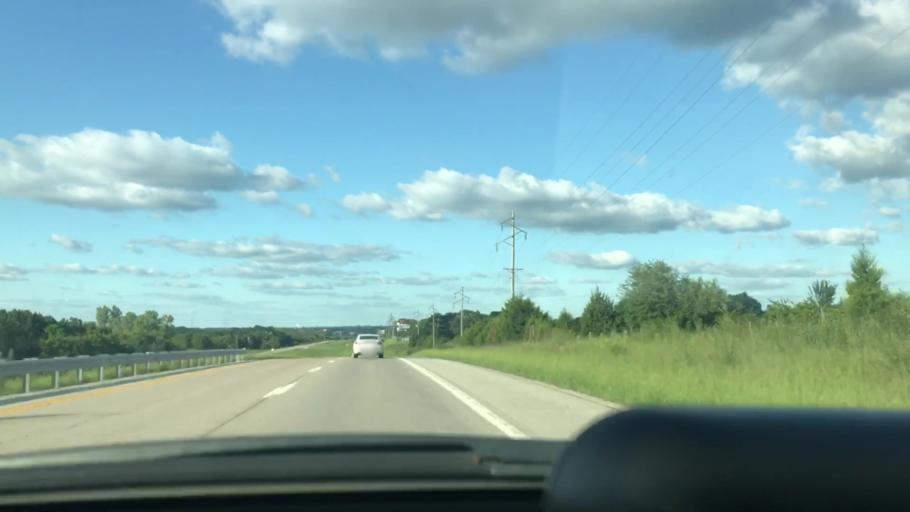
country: US
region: Missouri
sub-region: Pettis County
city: Sedalia
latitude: 38.6365
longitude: -93.2667
